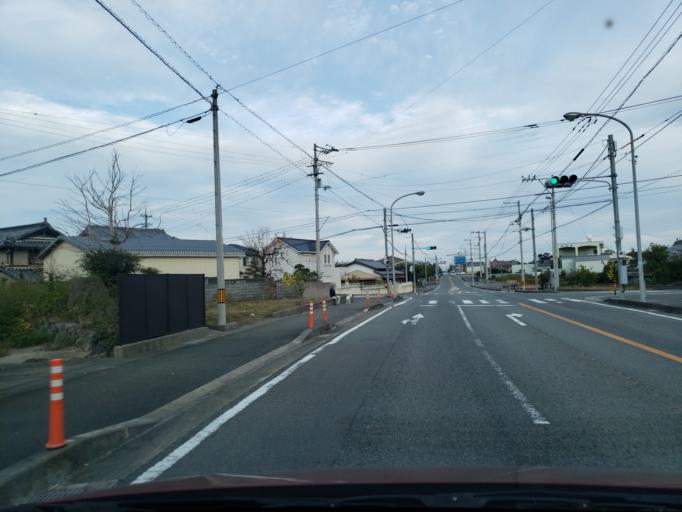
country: JP
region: Tokushima
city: Kamojimacho-jogejima
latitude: 34.0805
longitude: 134.2574
